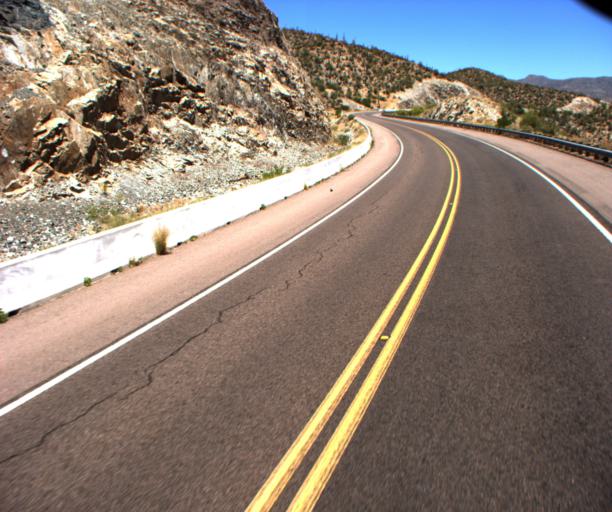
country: US
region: Arizona
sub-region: Pinal County
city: Kearny
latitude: 33.0735
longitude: -110.7223
